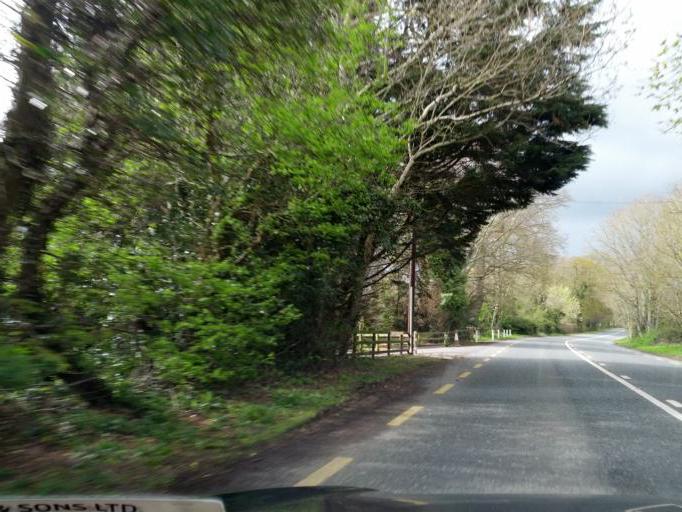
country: IE
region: Leinster
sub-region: An Mhi
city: Dunshaughlin
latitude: 53.5361
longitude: -6.5632
